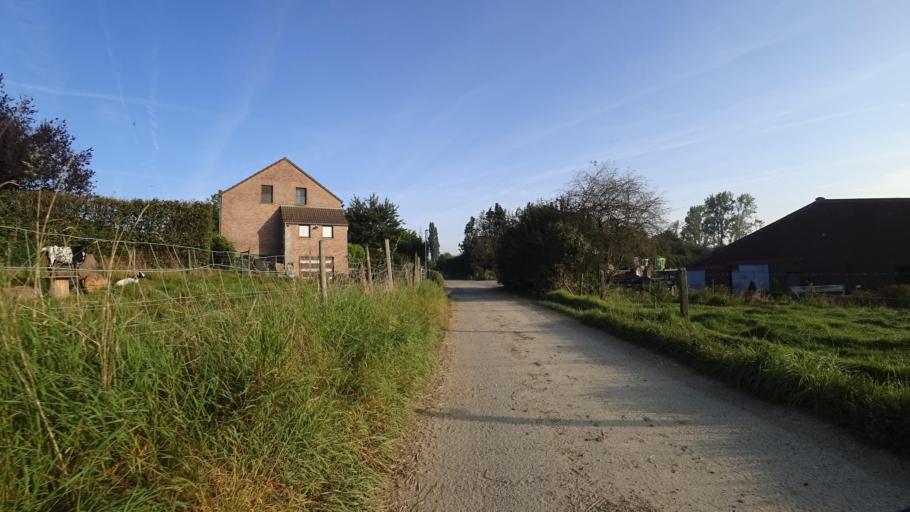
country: BE
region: Wallonia
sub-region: Province du Brabant Wallon
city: Walhain-Saint-Paul
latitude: 50.6582
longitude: 4.6742
